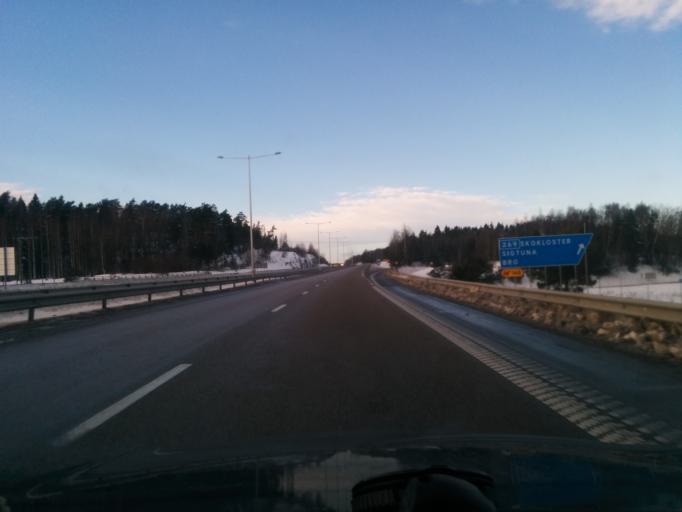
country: SE
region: Stockholm
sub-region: Upplands-Bro Kommun
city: Bro
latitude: 59.5305
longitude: 17.6324
